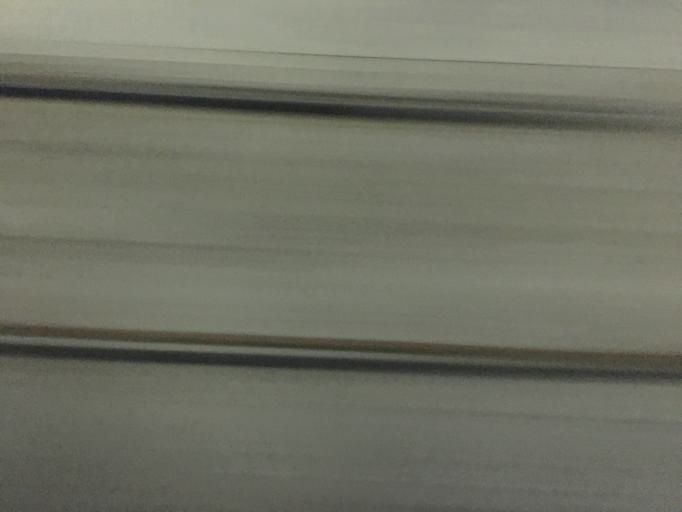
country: JP
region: Akita
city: Noshiromachi
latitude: 40.5867
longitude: 139.9187
